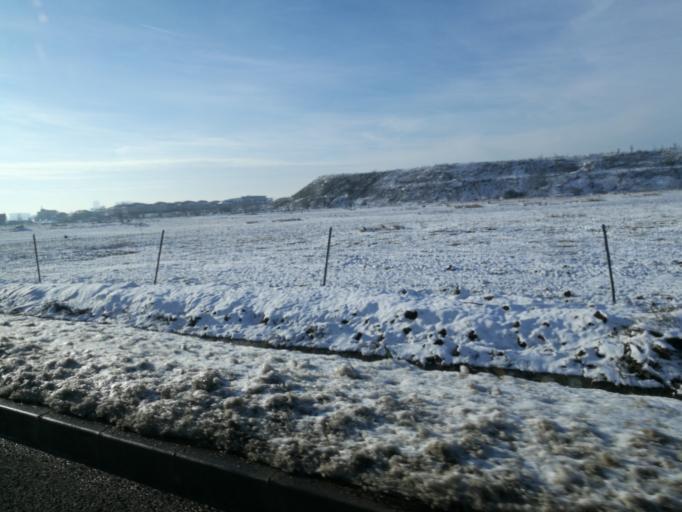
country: RO
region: Ilfov
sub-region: Voluntari City
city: Voluntari
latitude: 44.4983
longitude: 26.1528
